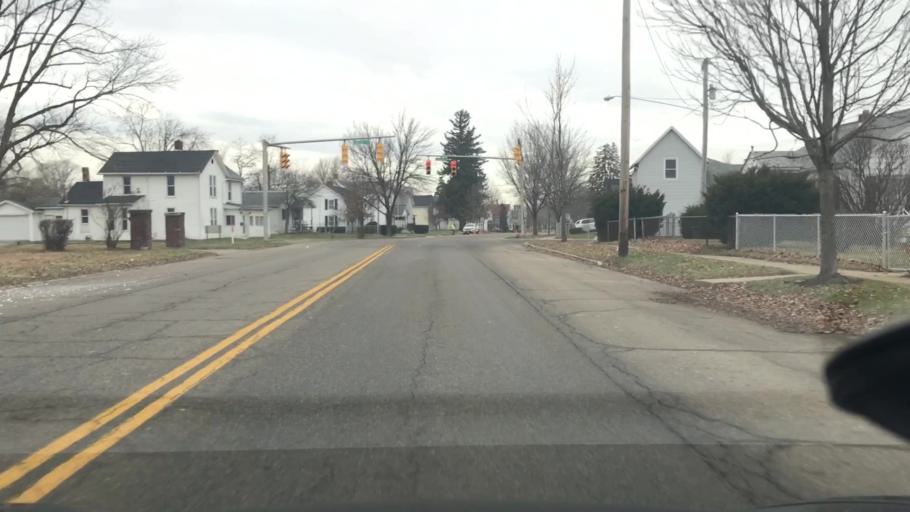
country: US
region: Ohio
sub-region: Madison County
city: London
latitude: 39.8802
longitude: -83.4399
